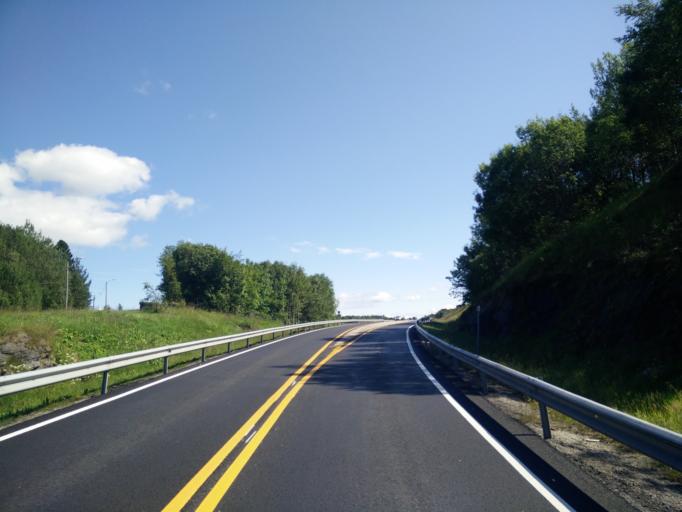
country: NO
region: More og Romsdal
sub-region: Kristiansund
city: Rensvik
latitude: 63.0259
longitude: 7.7658
